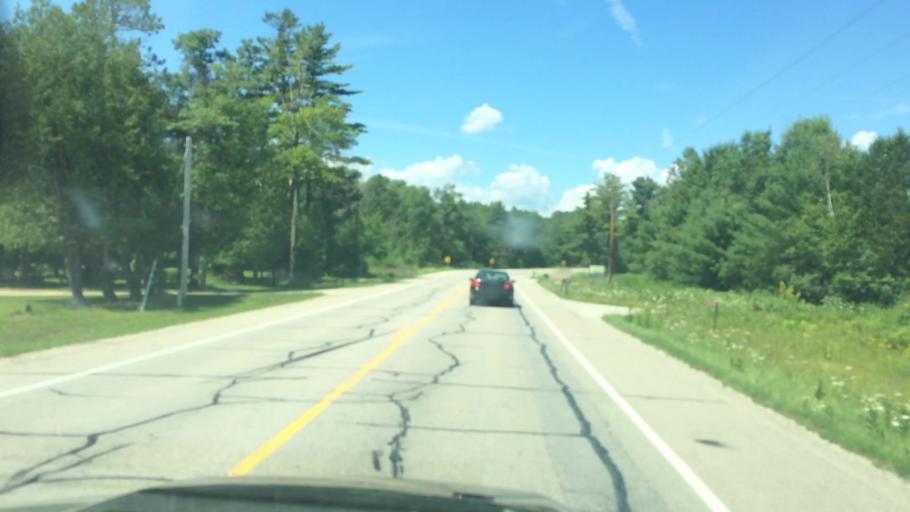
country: US
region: Wisconsin
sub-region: Marinette County
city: Peshtigo
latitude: 45.1005
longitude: -87.7407
